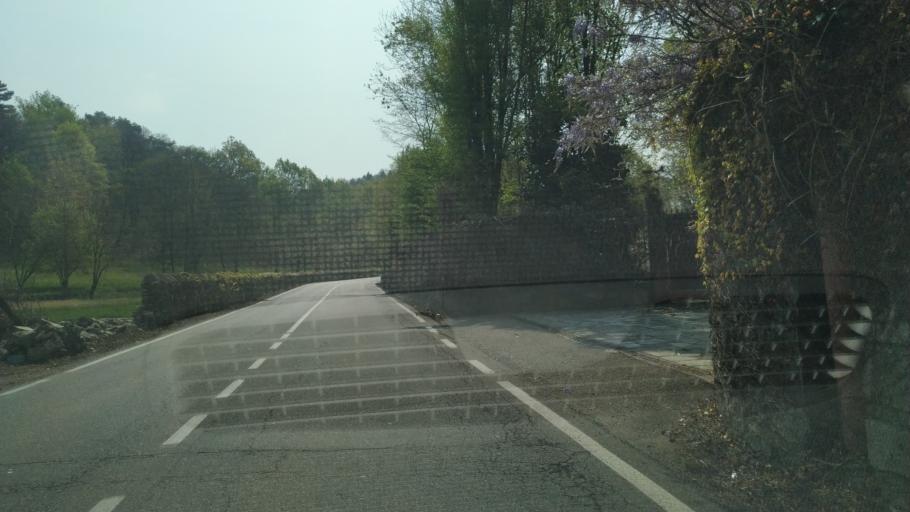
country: IT
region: Piedmont
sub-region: Provincia di Novara
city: Soriso
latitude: 45.7613
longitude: 8.4181
